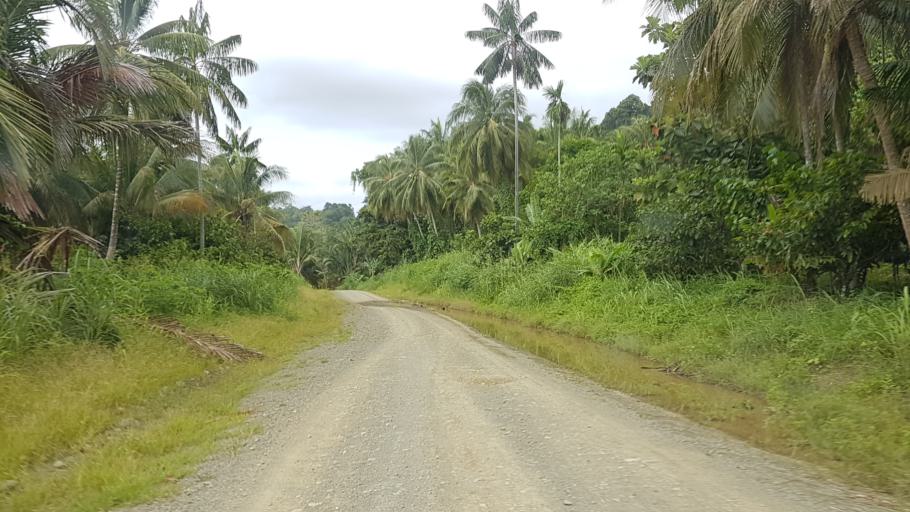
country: PG
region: East Sepik
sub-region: Wewak
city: Wewak
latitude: -3.3983
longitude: 143.2656
